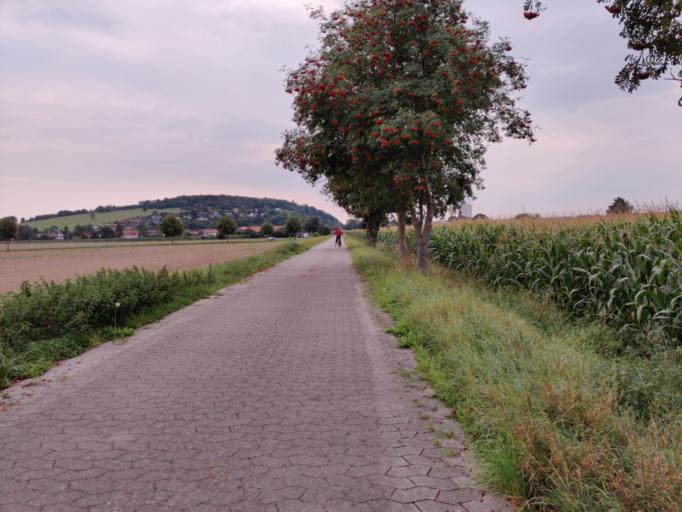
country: DE
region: Lower Saxony
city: Hameln
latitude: 52.0566
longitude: 9.3857
